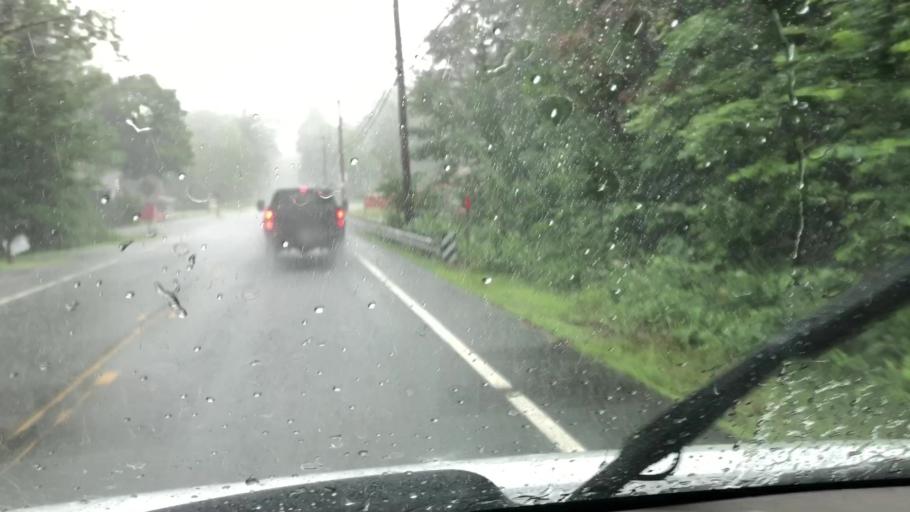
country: US
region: Massachusetts
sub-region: Hampshire County
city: Williamsburg
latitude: 42.4004
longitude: -72.7445
